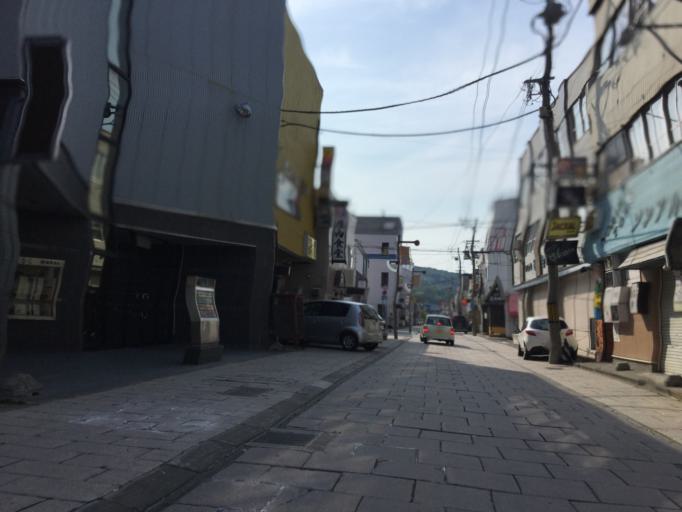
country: JP
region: Hokkaido
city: Wakkanai
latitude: 45.3977
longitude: 141.6859
